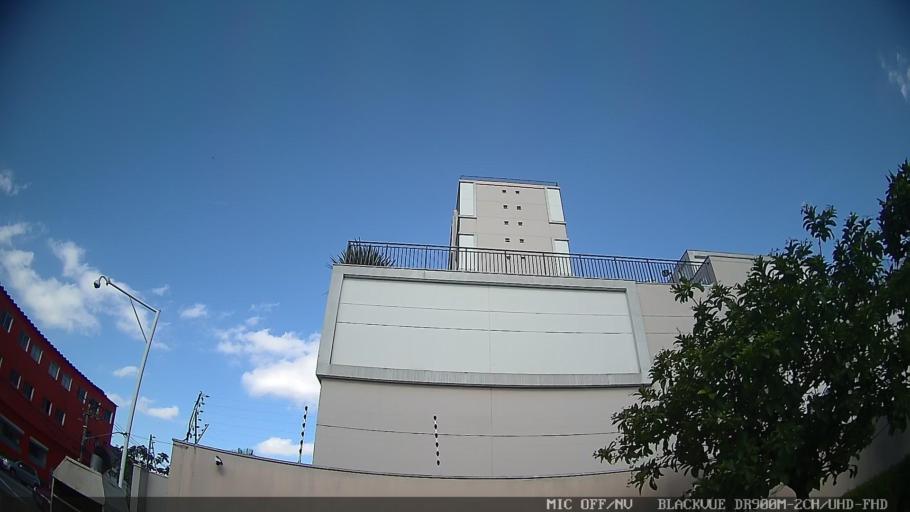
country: BR
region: Sao Paulo
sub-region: Sao Caetano Do Sul
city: Sao Caetano do Sul
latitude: -23.5959
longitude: -46.5996
